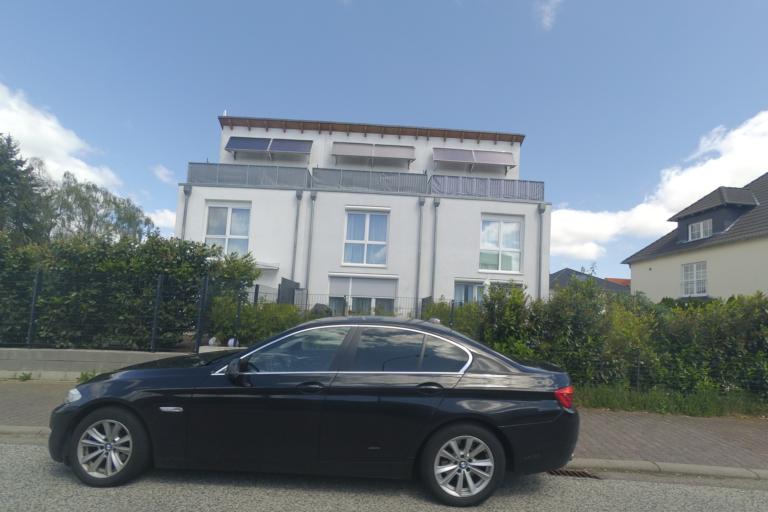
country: DE
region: Hesse
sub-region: Regierungsbezirk Darmstadt
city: Friedrichsdorf
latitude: 50.2543
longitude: 8.6794
